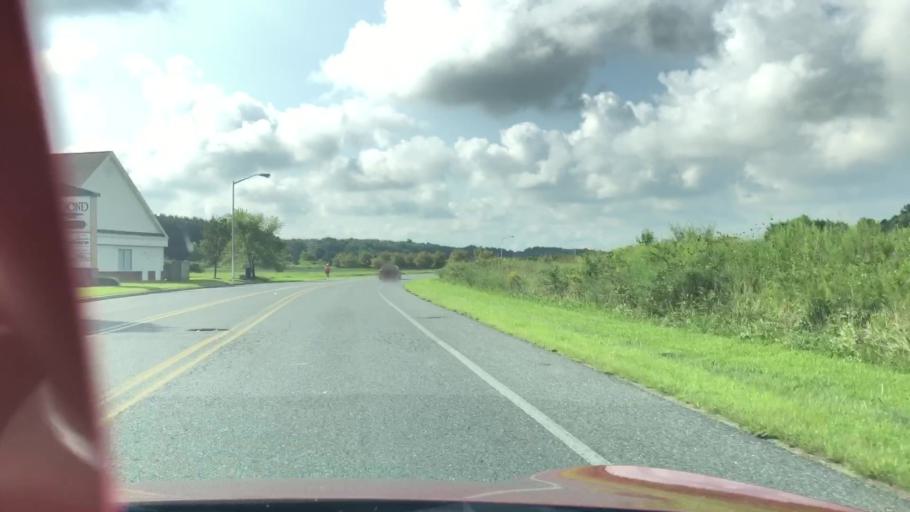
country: US
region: Maryland
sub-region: Wicomico County
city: Delmar
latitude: 38.4067
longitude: -75.5631
